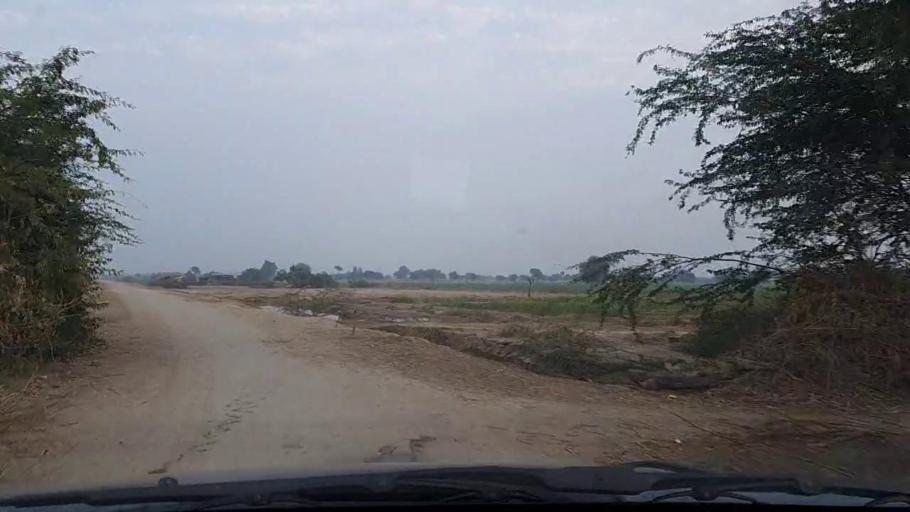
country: PK
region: Sindh
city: Pithoro
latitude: 25.6285
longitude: 69.4336
